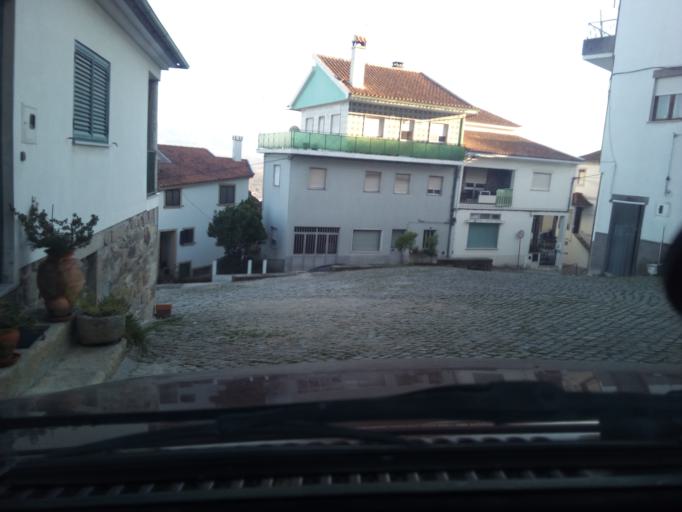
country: PT
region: Guarda
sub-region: Fornos de Algodres
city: Fornos de Algodres
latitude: 40.6213
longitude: -7.5389
